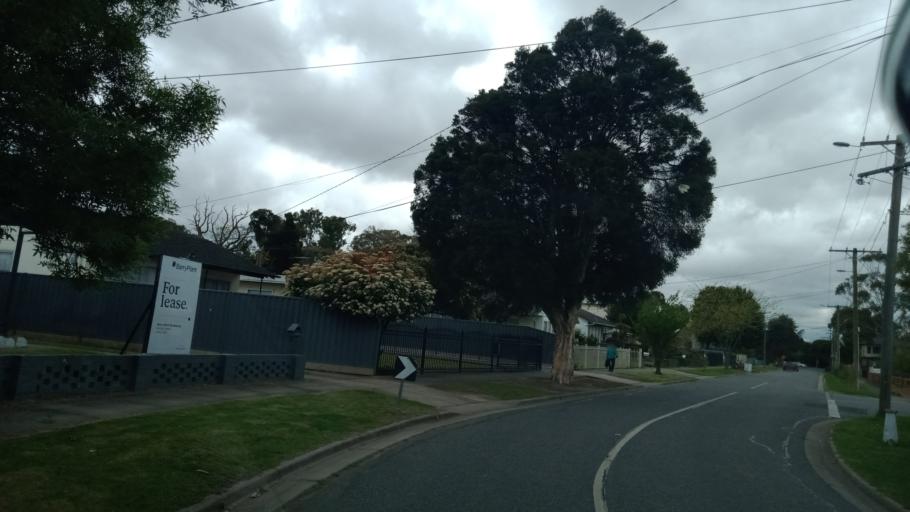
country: AU
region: Victoria
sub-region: Casey
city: Doveton
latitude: -37.9918
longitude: 145.2307
